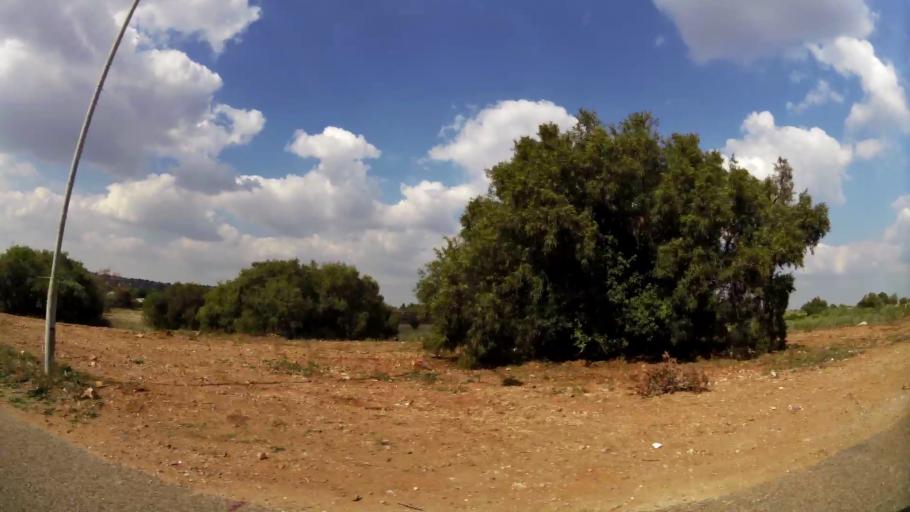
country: ZA
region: Gauteng
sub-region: City of Tshwane Metropolitan Municipality
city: Centurion
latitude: -25.8265
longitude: 28.2363
